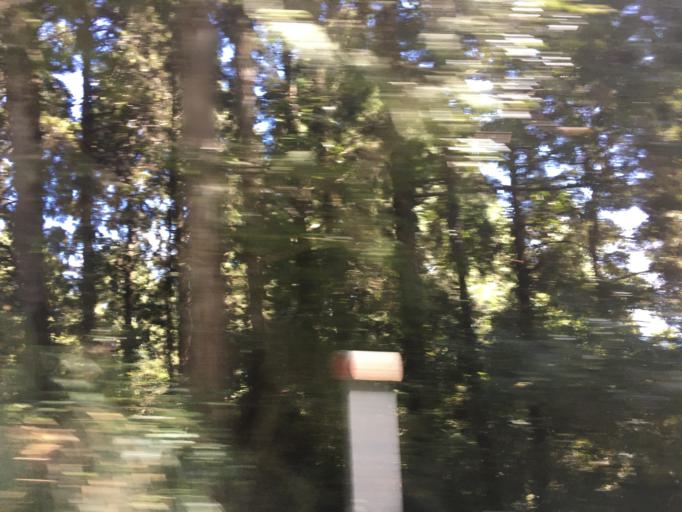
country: TW
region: Taiwan
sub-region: Yilan
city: Yilan
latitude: 24.5224
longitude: 121.5209
